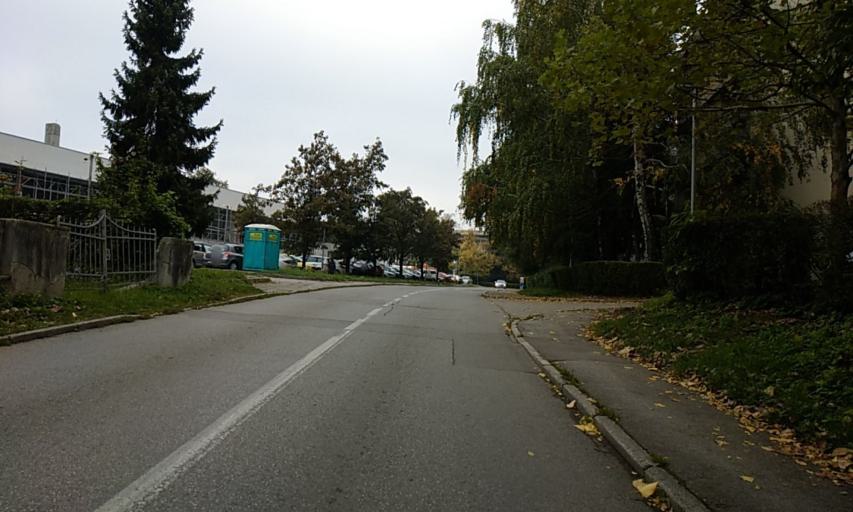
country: BA
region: Republika Srpska
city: Mejdan - Obilicevo
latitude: 44.7680
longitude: 17.1940
